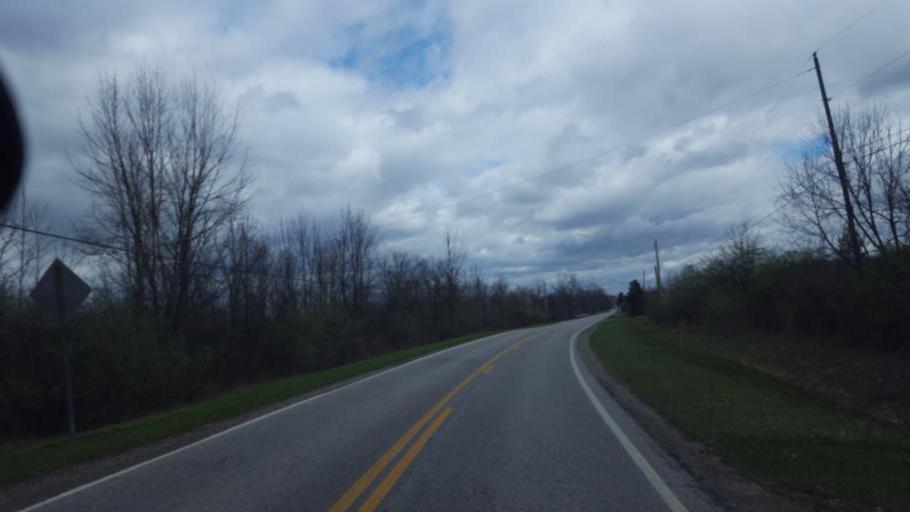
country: US
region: Ohio
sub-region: Franklin County
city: Westerville
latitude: 40.1547
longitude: -82.8705
